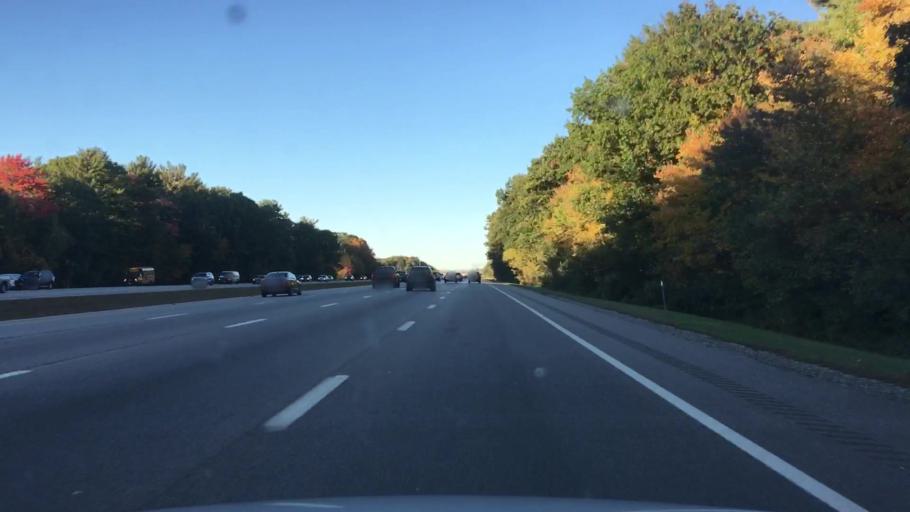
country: US
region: New Hampshire
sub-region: Rockingham County
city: Greenland
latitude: 43.0118
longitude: -70.8360
